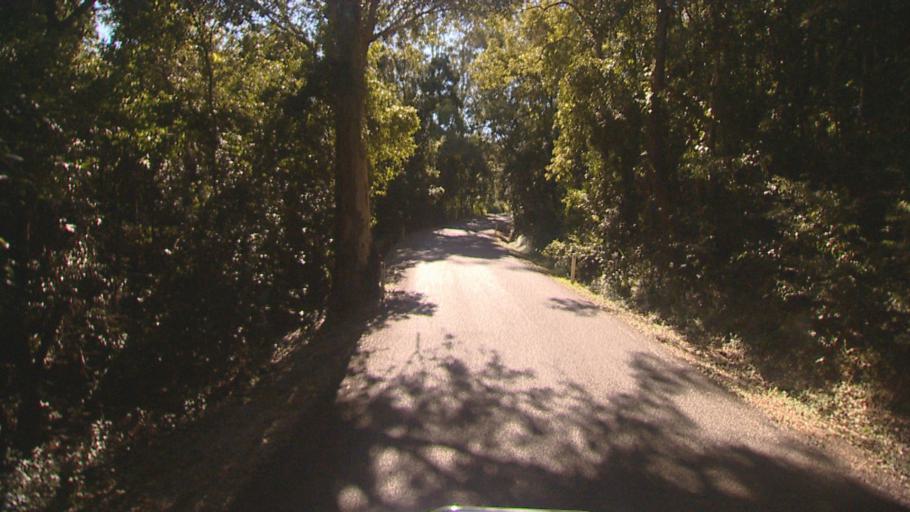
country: AU
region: Queensland
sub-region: Logan
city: Slacks Creek
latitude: -27.6616
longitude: 153.1615
